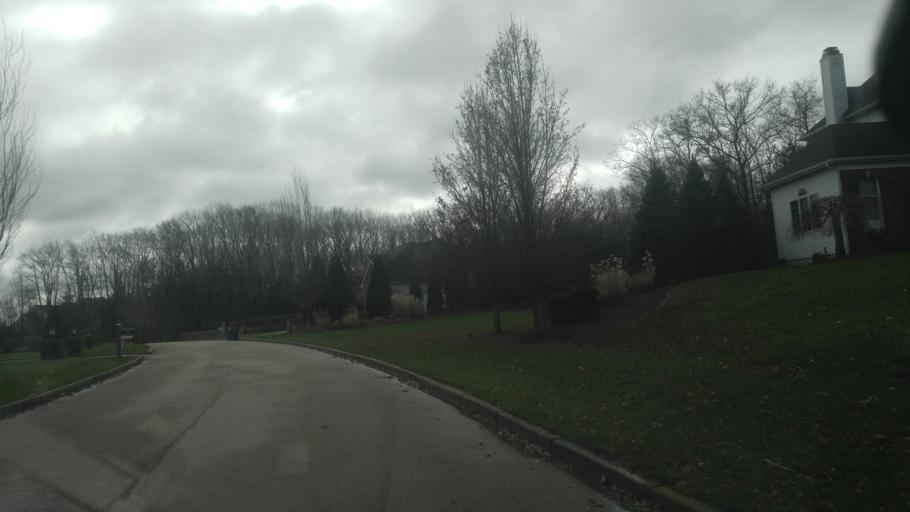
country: US
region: Rhode Island
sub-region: Washington County
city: Exeter
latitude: 41.6377
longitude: -71.5354
